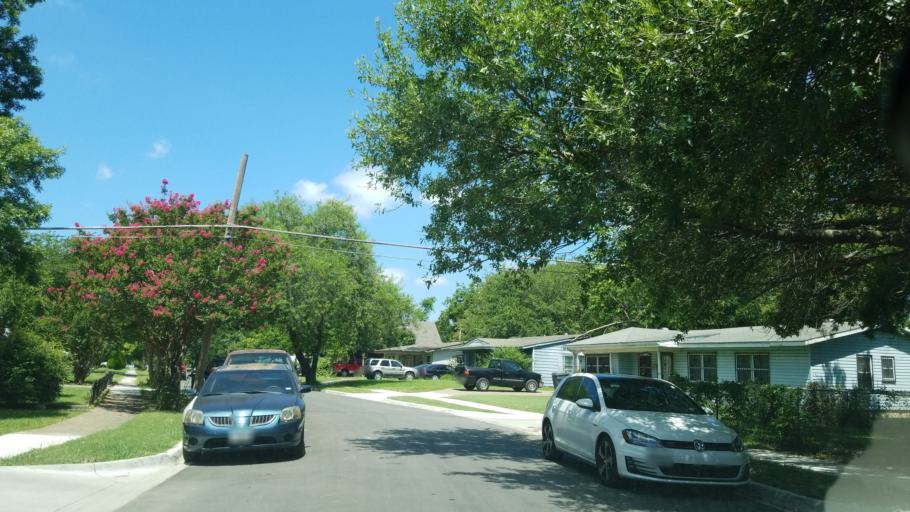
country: US
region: Texas
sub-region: Dallas County
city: Balch Springs
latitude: 32.7355
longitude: -96.6957
